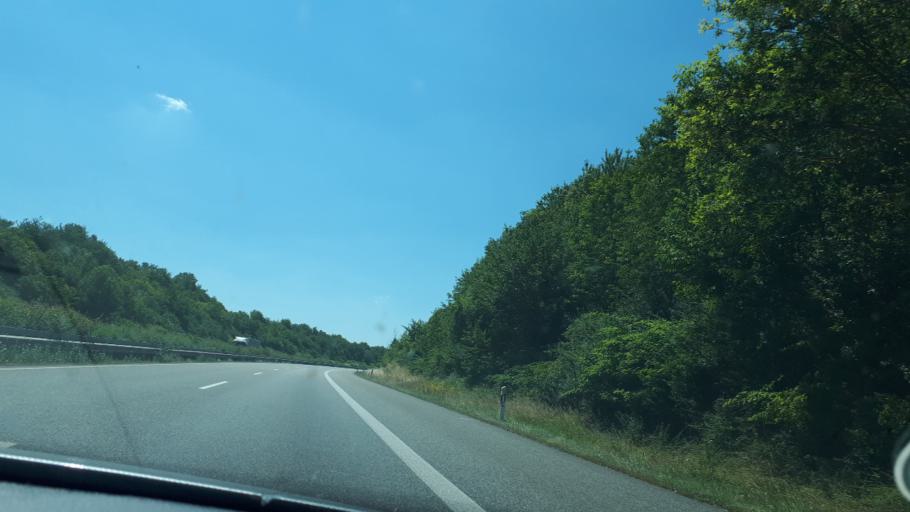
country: DE
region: Rheinland-Pfalz
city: Trimbs
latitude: 50.3070
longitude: 7.2910
